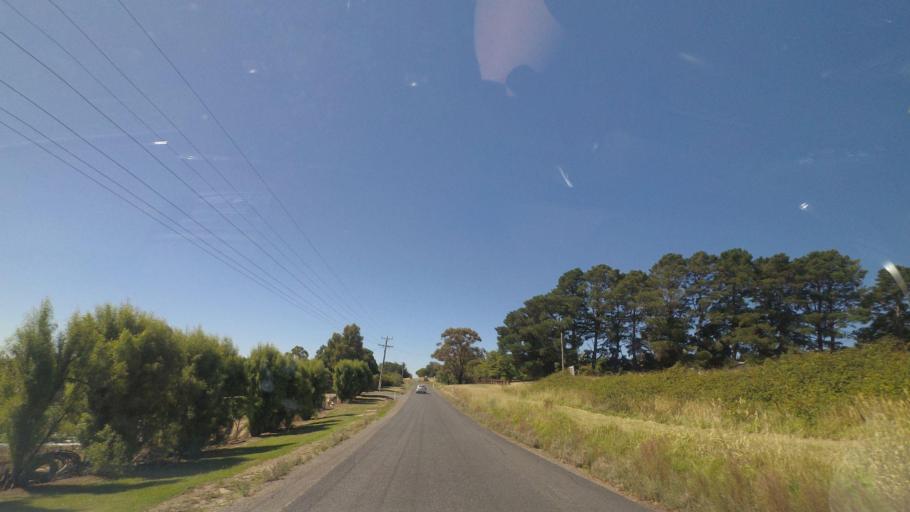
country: AU
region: Victoria
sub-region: Yarra Ranges
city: Chirnside Park
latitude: -37.7435
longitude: 145.3243
